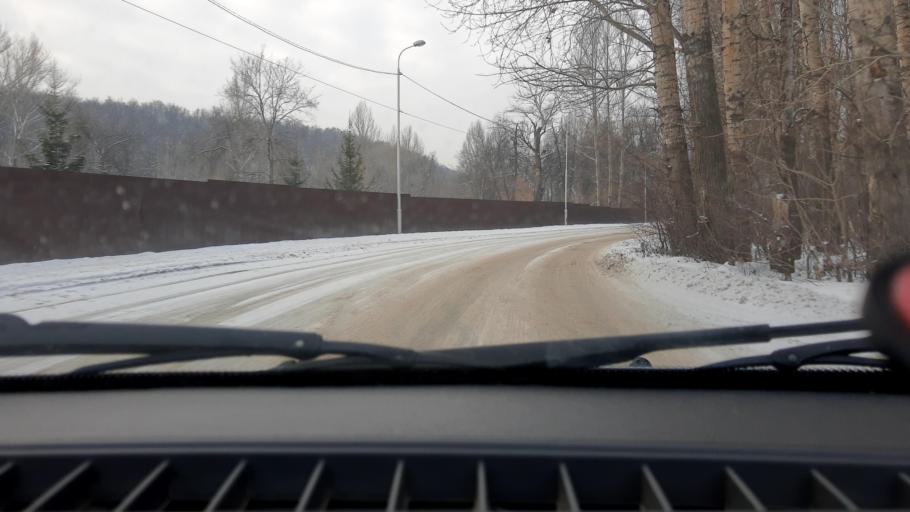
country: RU
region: Bashkortostan
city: Ufa
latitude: 54.8108
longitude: 56.0406
